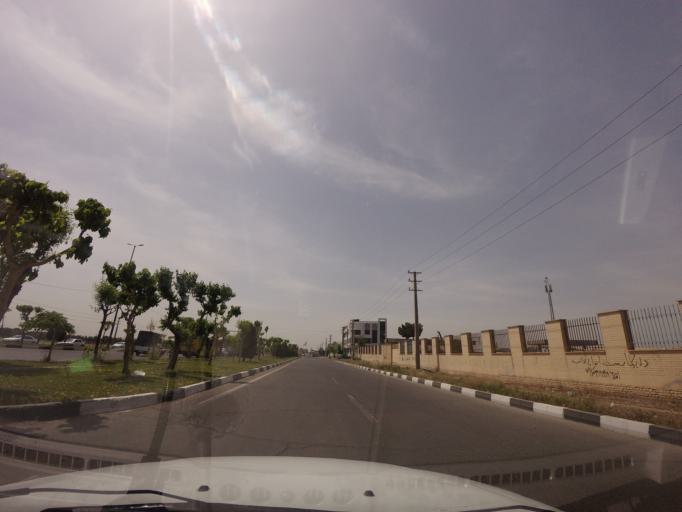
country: IR
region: Tehran
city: Eslamshahr
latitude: 35.5698
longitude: 51.2616
